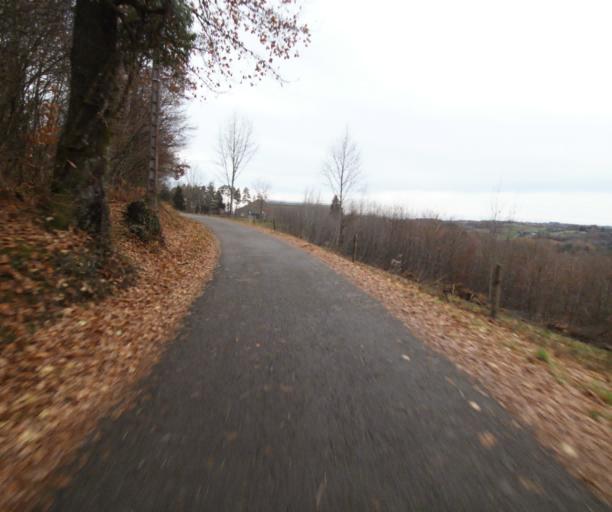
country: FR
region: Limousin
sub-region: Departement de la Correze
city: Chameyrat
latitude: 45.2339
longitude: 1.6540
